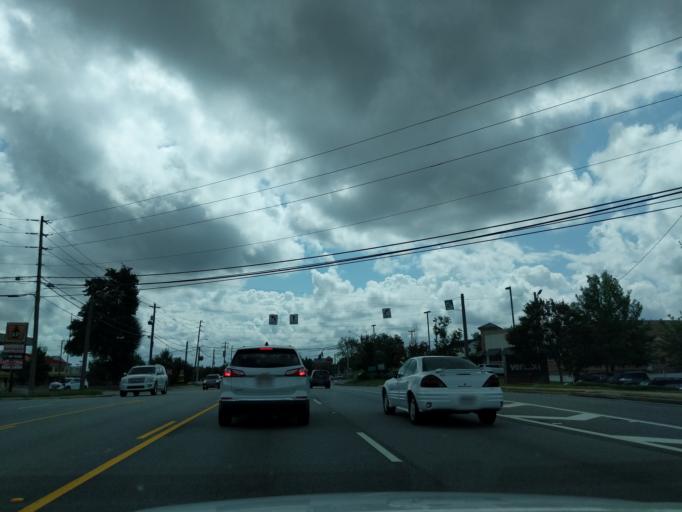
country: US
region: Georgia
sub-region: Columbia County
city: Evans
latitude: 33.5380
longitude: -82.1295
